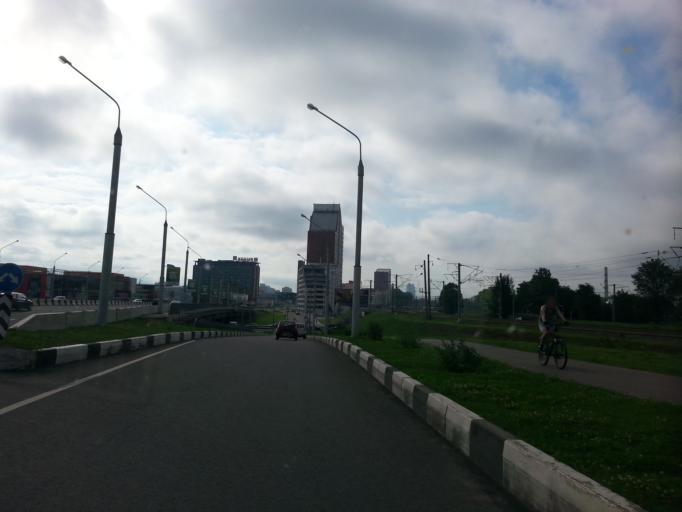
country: BY
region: Minsk
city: Minsk
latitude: 53.9277
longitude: 27.5035
